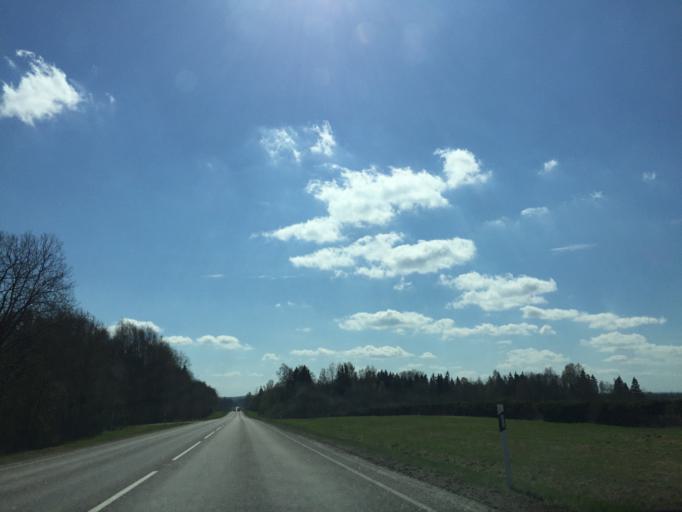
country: EE
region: Tartu
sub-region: Elva linn
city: Elva
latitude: 58.1080
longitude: 26.2380
